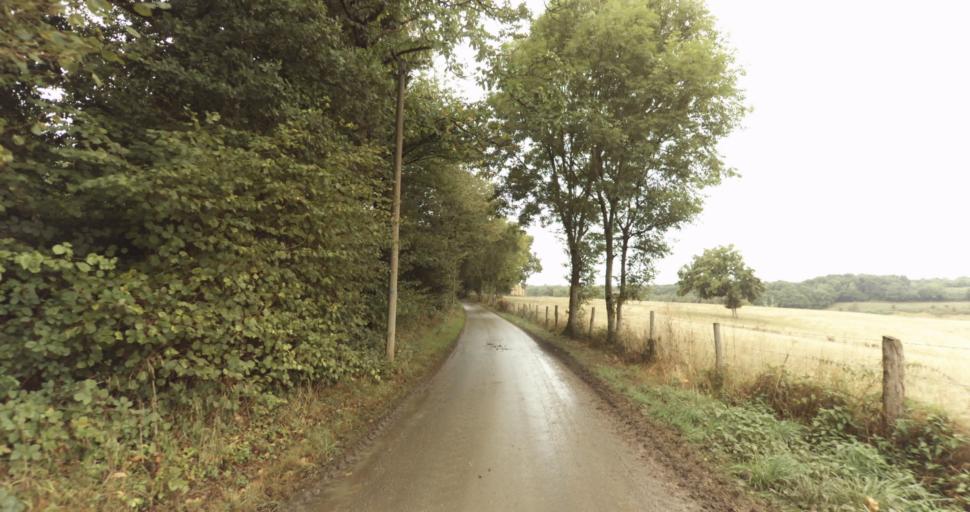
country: FR
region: Lower Normandy
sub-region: Departement de l'Orne
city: Vimoutiers
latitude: 48.8634
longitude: 0.1957
